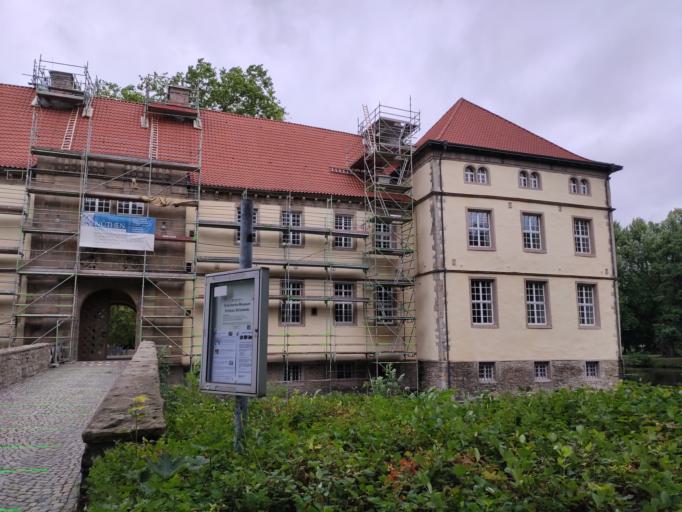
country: DE
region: North Rhine-Westphalia
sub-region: Regierungsbezirk Arnsberg
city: Herne
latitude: 51.5510
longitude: 7.2114
